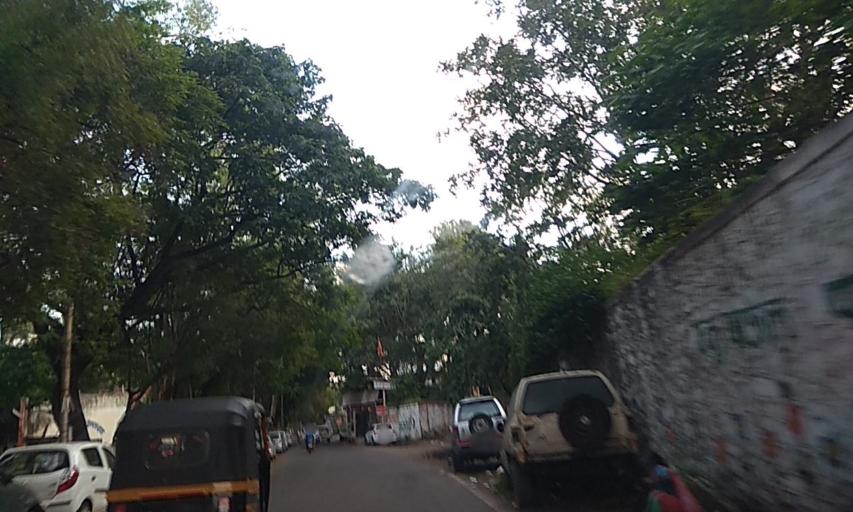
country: IN
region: Maharashtra
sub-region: Pune Division
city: Pune
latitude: 18.4962
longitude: 73.8510
